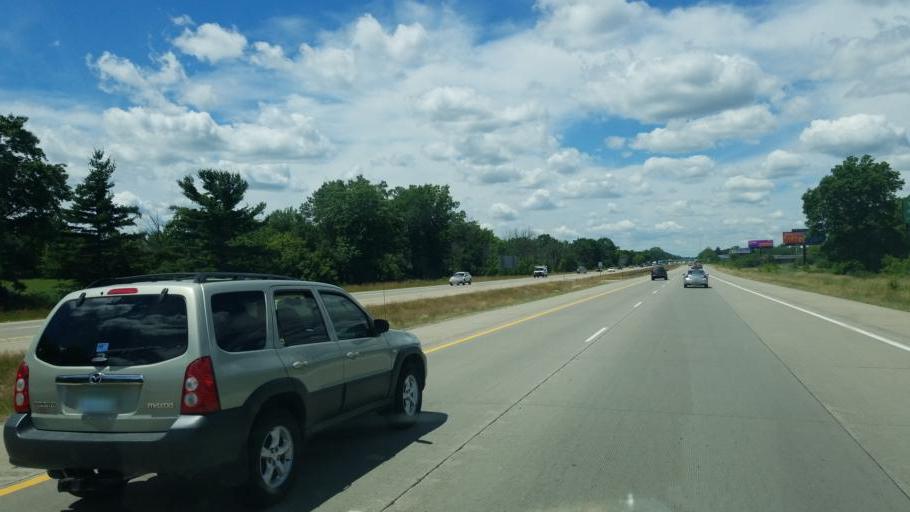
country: US
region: Michigan
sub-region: Ingham County
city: Okemos
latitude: 42.6782
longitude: -84.4492
